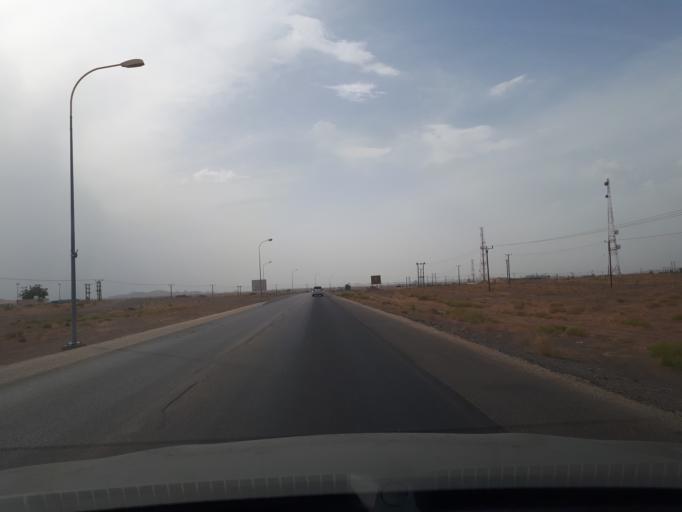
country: OM
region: Ash Sharqiyah
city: Al Qabil
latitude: 22.5079
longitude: 58.7433
